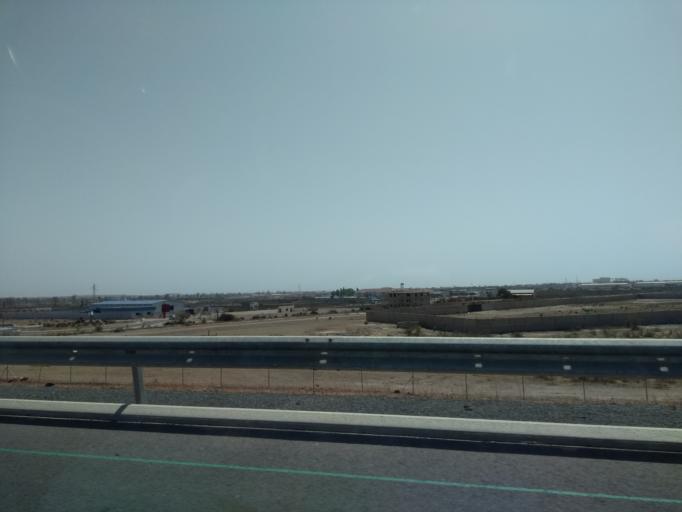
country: SN
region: Thies
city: Pout
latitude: 14.7328
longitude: -17.1606
